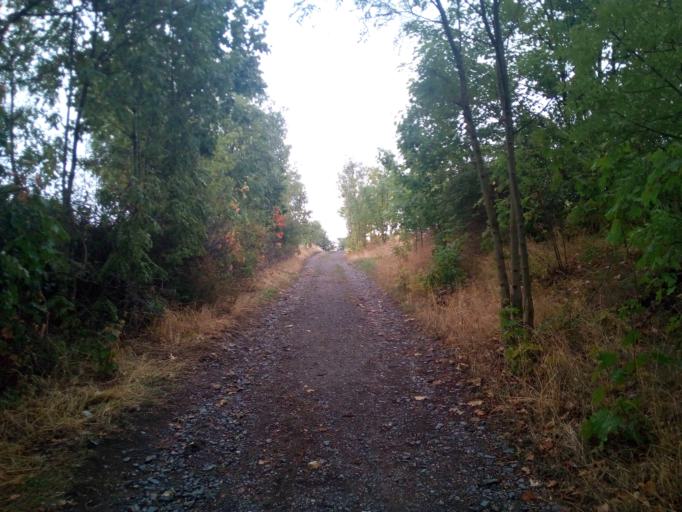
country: DE
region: Saxony
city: Kreischa
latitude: 50.9275
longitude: 13.7951
